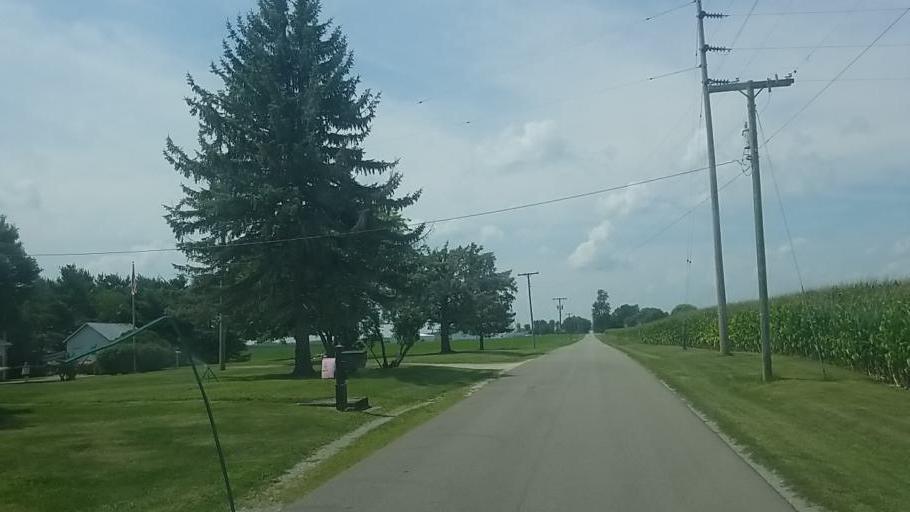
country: US
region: Ohio
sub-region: Marion County
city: Marion
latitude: 40.6734
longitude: -83.2164
